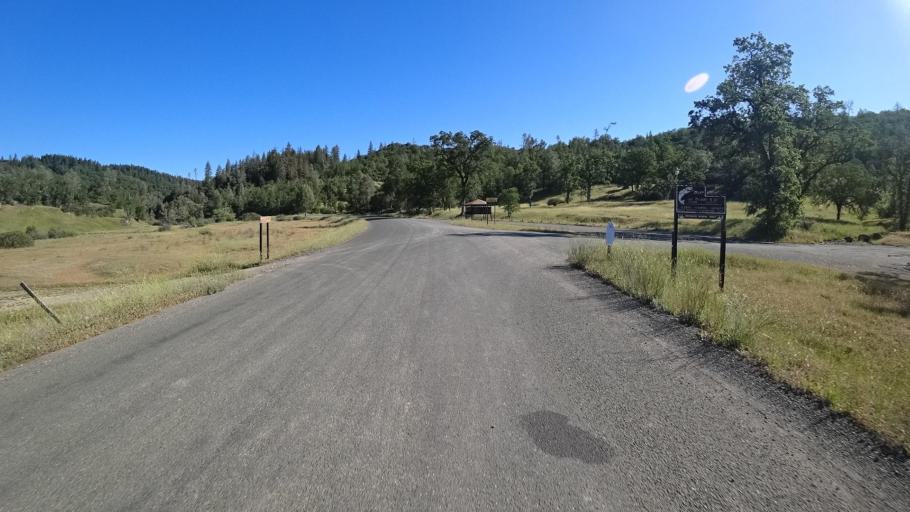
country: US
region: California
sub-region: Lake County
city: Upper Lake
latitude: 39.4133
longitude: -122.9744
